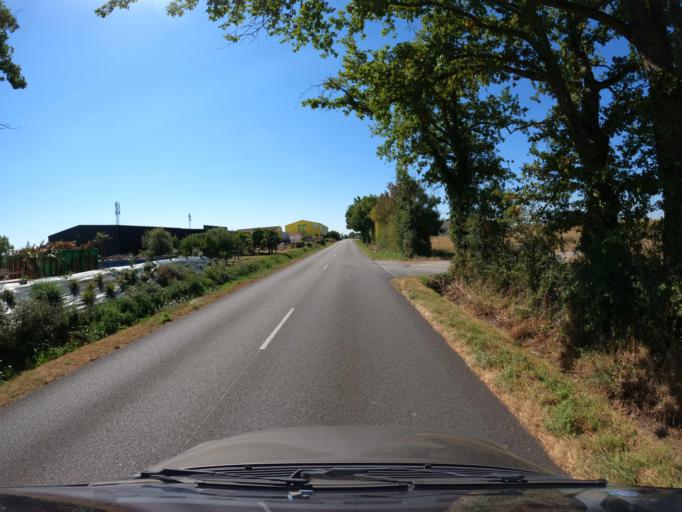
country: FR
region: Pays de la Loire
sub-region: Departement de la Vendee
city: La Boissiere-de-Montaigu
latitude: 46.9494
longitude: -1.2005
